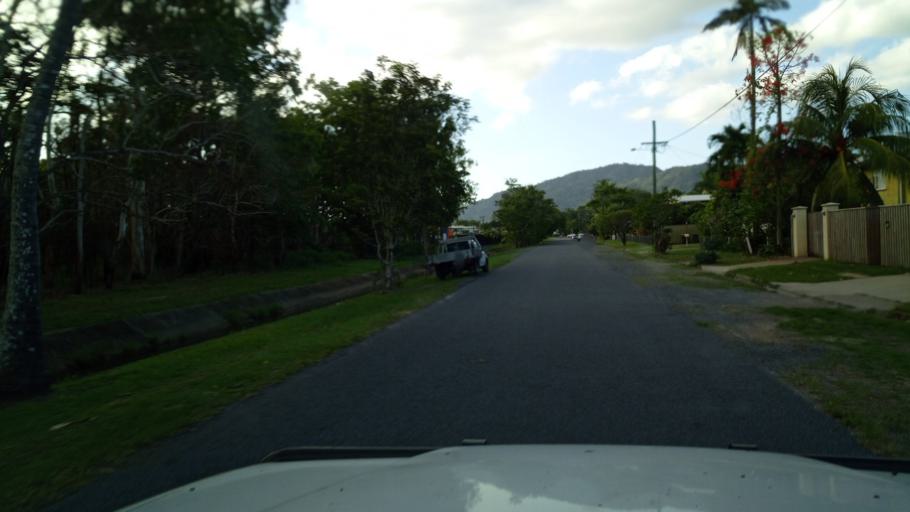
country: AU
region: Queensland
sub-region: Cairns
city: Cairns
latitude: -16.9163
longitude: 145.7542
